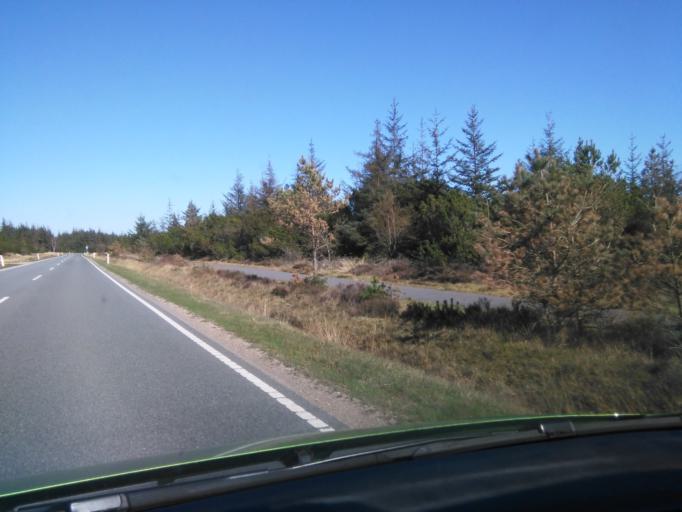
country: DK
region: South Denmark
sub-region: Varde Kommune
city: Oksbol
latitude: 55.5664
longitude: 8.1795
